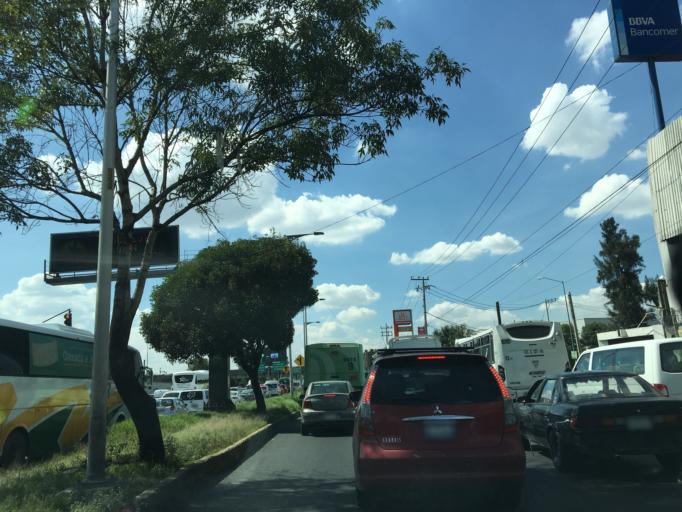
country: MX
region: Mexico City
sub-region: Iztacalco
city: Iztacalco
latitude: 19.4077
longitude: -99.0743
